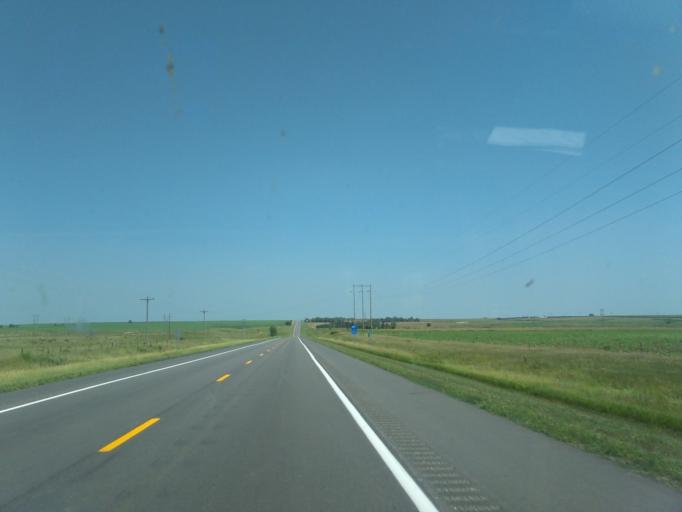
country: US
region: Nebraska
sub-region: Red Willow County
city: McCook
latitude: 40.2858
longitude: -100.6498
